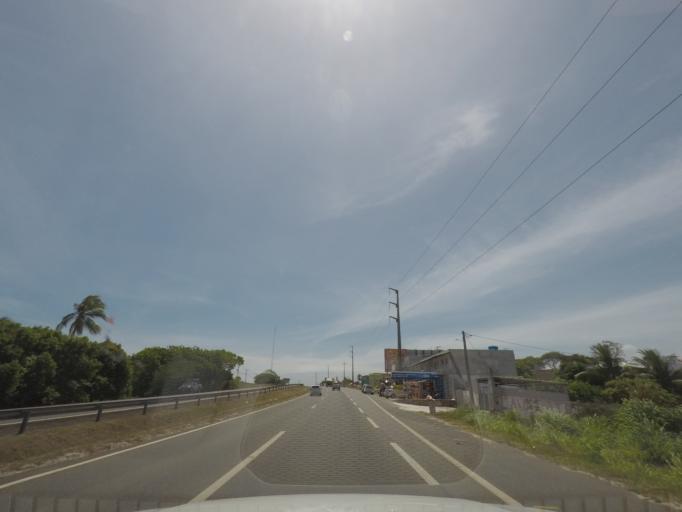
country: BR
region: Bahia
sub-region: Camacari
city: Camacari
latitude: -12.6890
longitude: -38.1187
